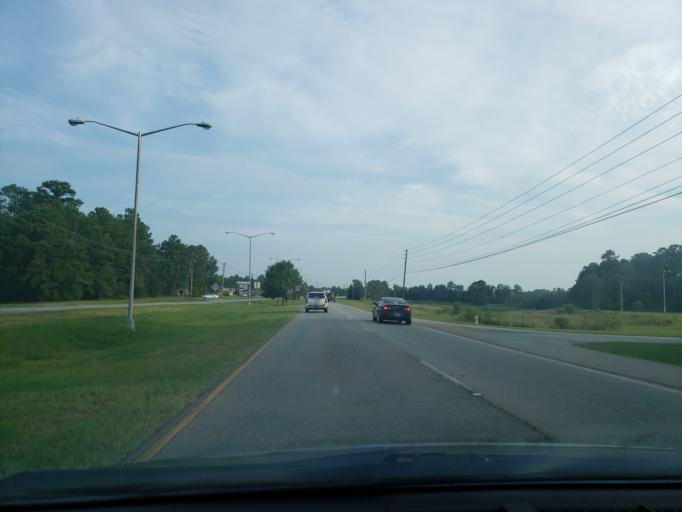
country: US
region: Georgia
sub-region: Dougherty County
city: Albany
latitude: 31.6039
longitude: -84.2208
